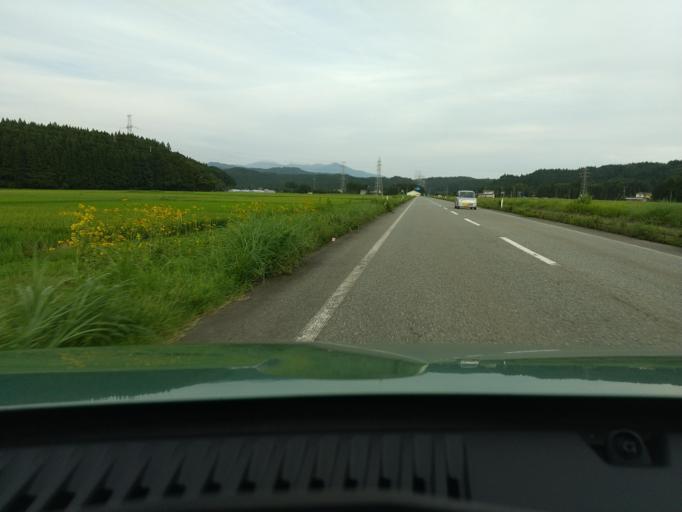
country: JP
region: Akita
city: Akita Shi
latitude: 39.7931
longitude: 140.1060
